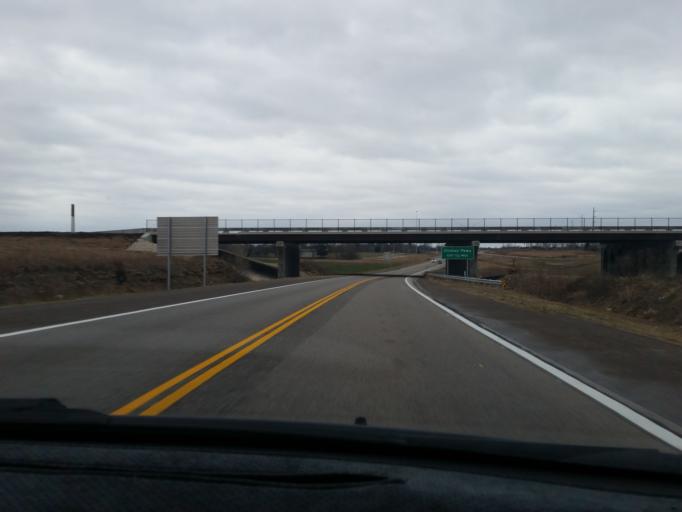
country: US
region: Kansas
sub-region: Douglas County
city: Lawrence
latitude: 38.9608
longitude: -95.3341
